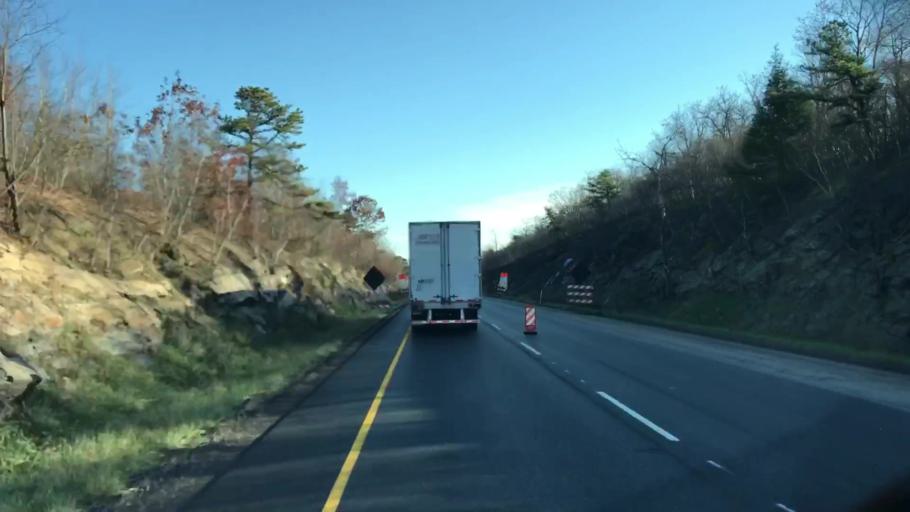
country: US
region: Pennsylvania
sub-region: Schuylkill County
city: Mahanoy City
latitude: 40.8285
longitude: -76.0718
